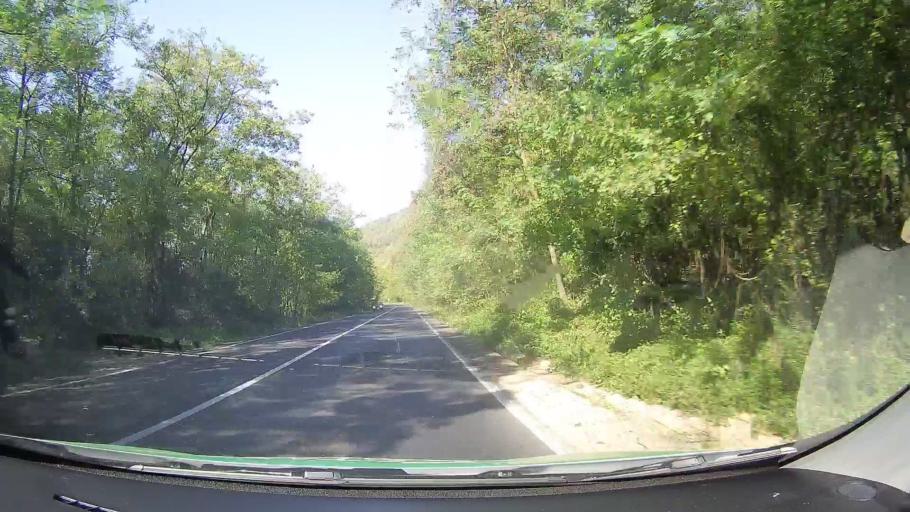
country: RO
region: Arad
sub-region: Comuna Savarsin
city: Savarsin
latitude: 46.0097
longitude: 22.2711
